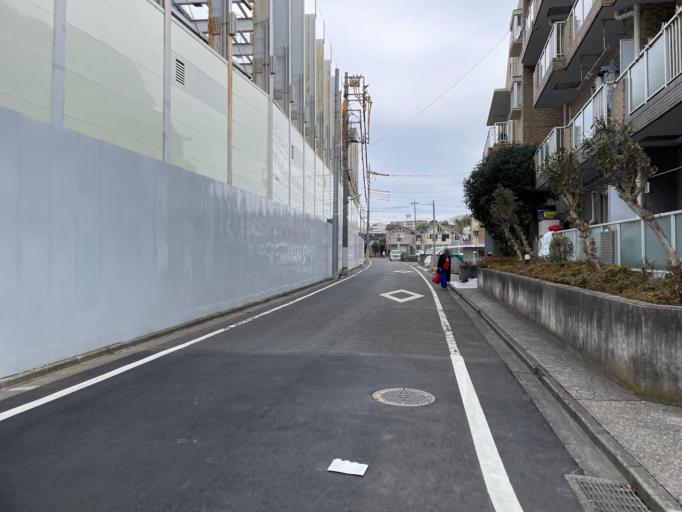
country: JP
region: Tokyo
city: Chofugaoka
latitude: 35.6279
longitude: 139.6064
